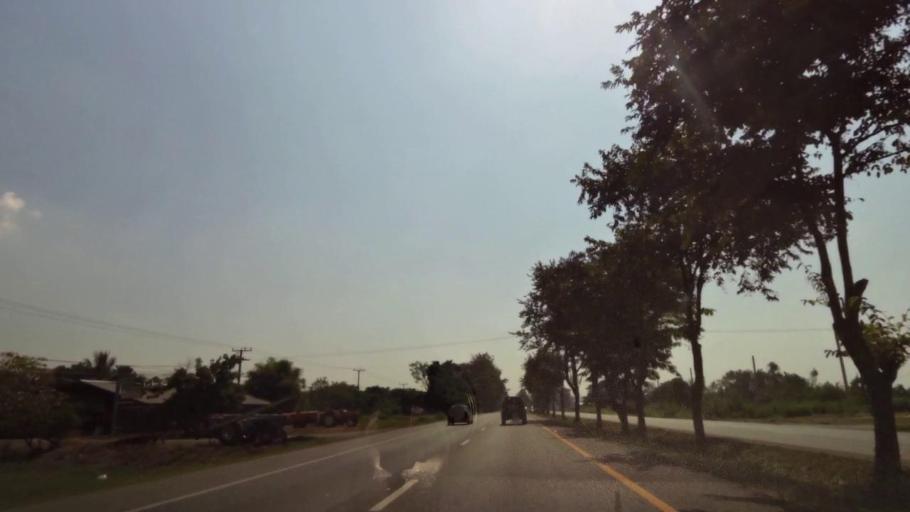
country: TH
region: Phichit
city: Bueng Na Rang
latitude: 16.0930
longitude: 100.1253
